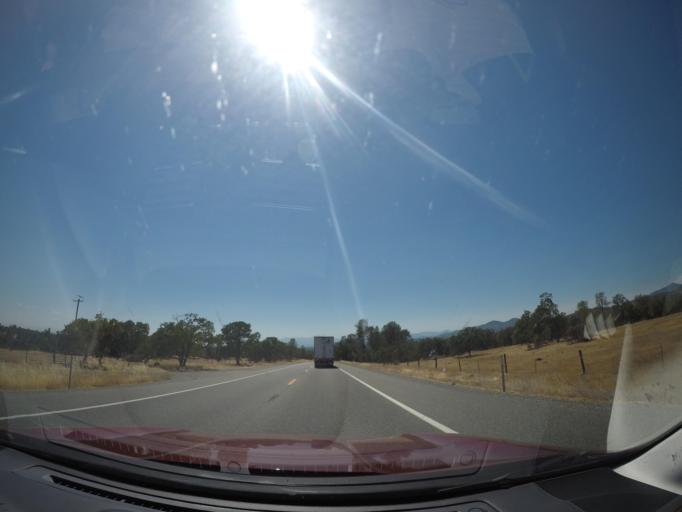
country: US
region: California
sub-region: Shasta County
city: Bella Vista
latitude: 40.6883
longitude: -122.1286
